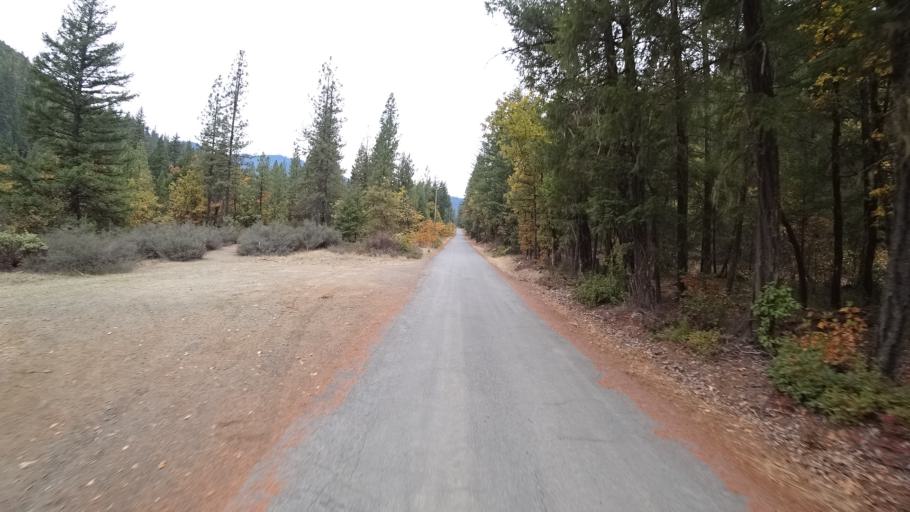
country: US
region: California
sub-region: Siskiyou County
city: Happy Camp
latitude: 41.8808
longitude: -123.4324
